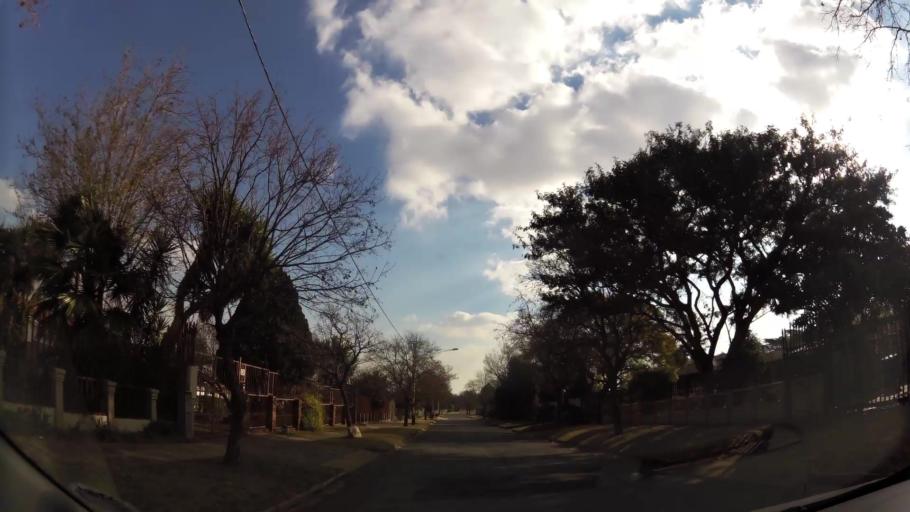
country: ZA
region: Gauteng
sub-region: West Rand District Municipality
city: Krugersdorp
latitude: -26.0925
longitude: 27.7655
